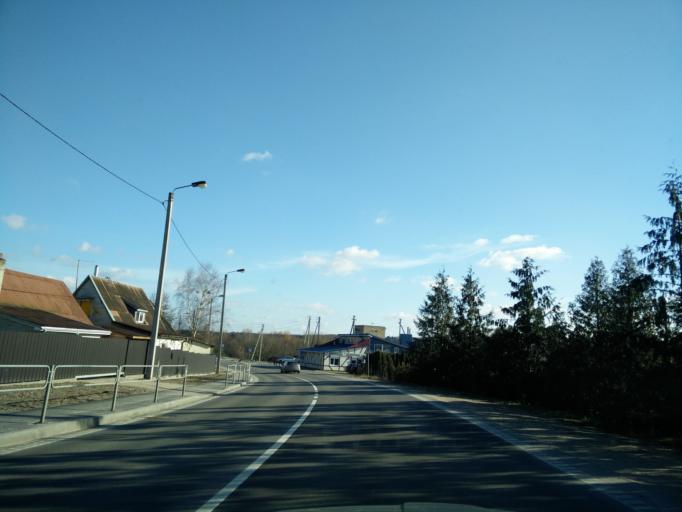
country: LT
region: Kauno apskritis
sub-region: Kauno rajonas
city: Akademija (Kaunas)
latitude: 54.9235
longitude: 23.7937
